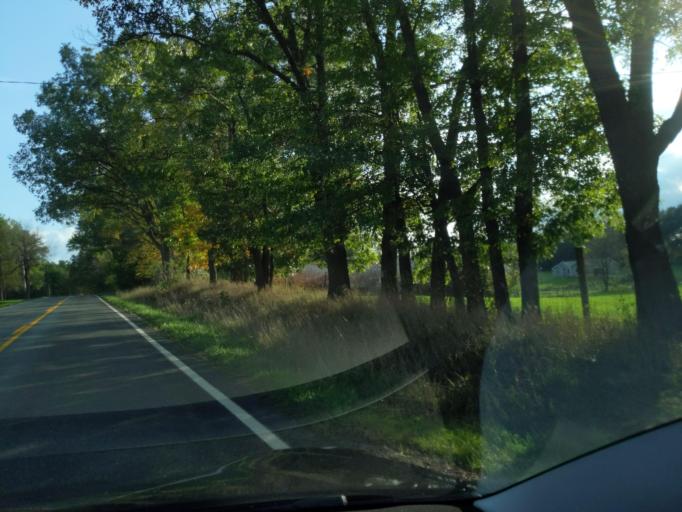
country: US
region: Michigan
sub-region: Ingham County
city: Leslie
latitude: 42.3618
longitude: -84.4629
